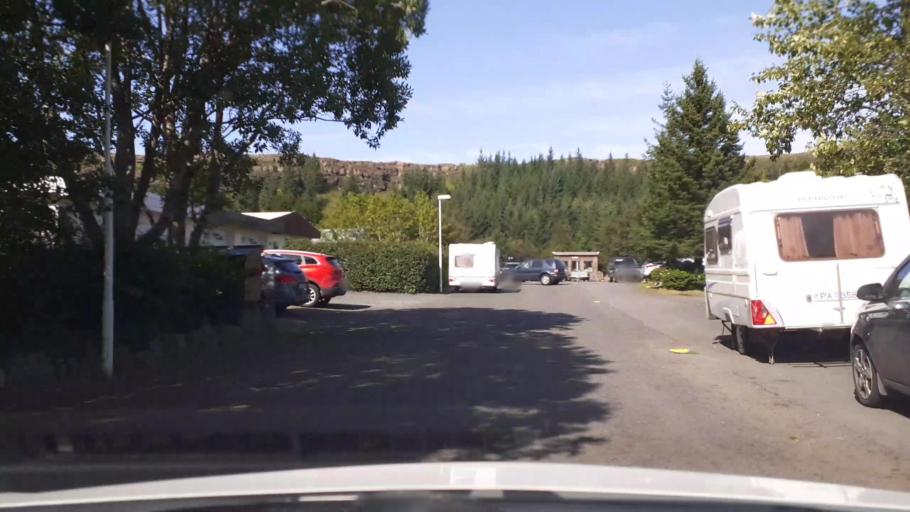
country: IS
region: South
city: Hveragerdi
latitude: 64.0043
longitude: -21.2026
